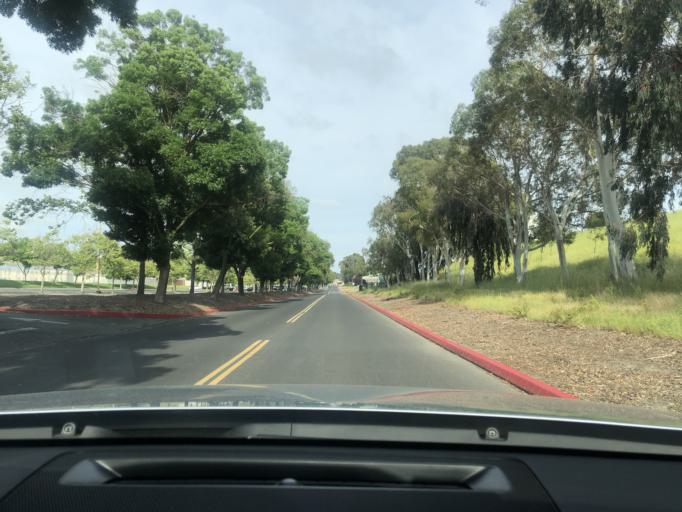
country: US
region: California
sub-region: Alameda County
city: Dublin
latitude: 37.7159
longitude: -121.8917
